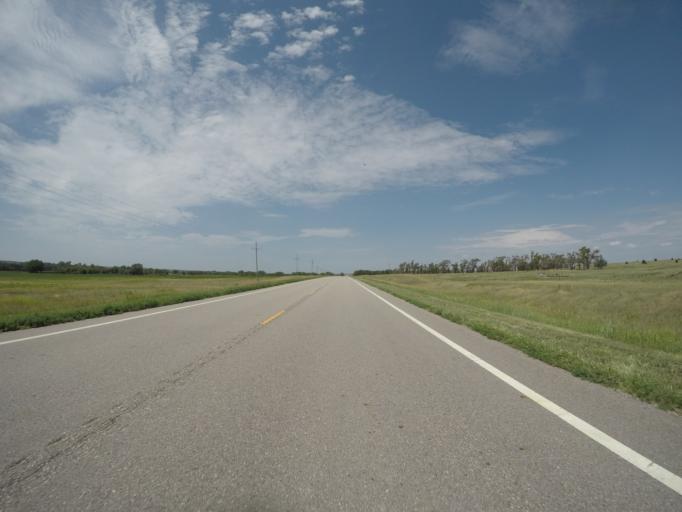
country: US
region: Kansas
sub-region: Rooks County
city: Stockton
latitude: 39.4444
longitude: -99.1816
